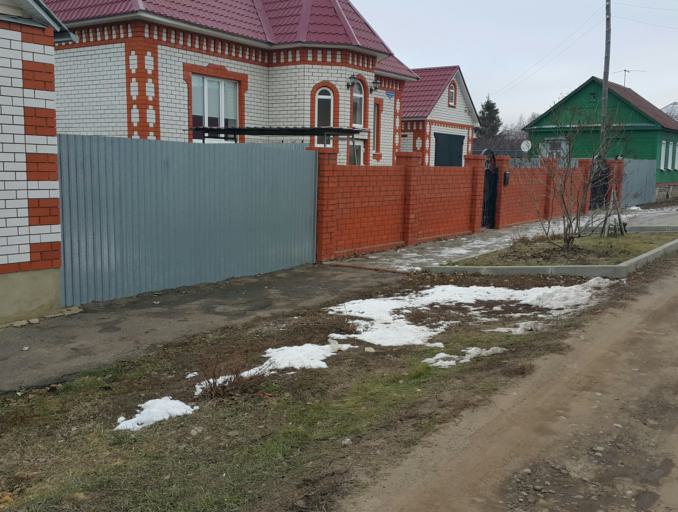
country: RU
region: Tambov
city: Tambov
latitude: 52.7256
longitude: 41.4017
